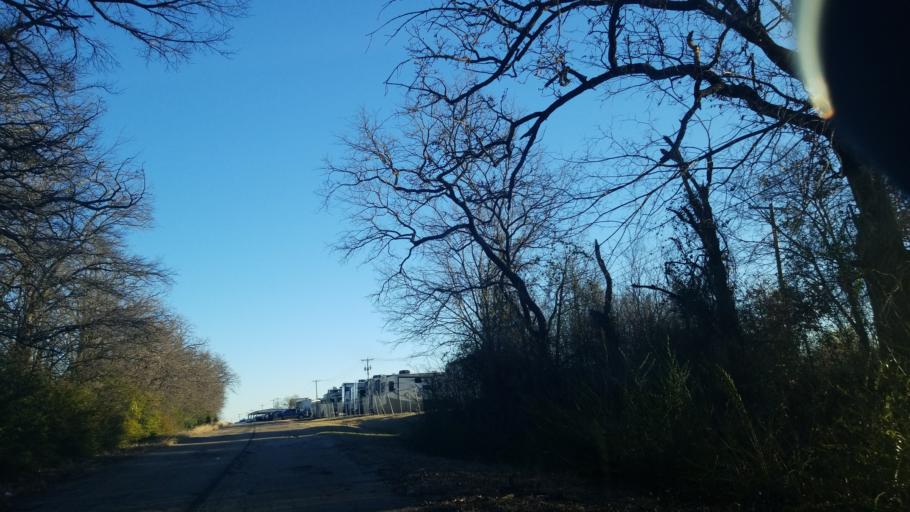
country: US
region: Texas
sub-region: Denton County
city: Corinth
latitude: 33.1600
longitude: -97.0665
